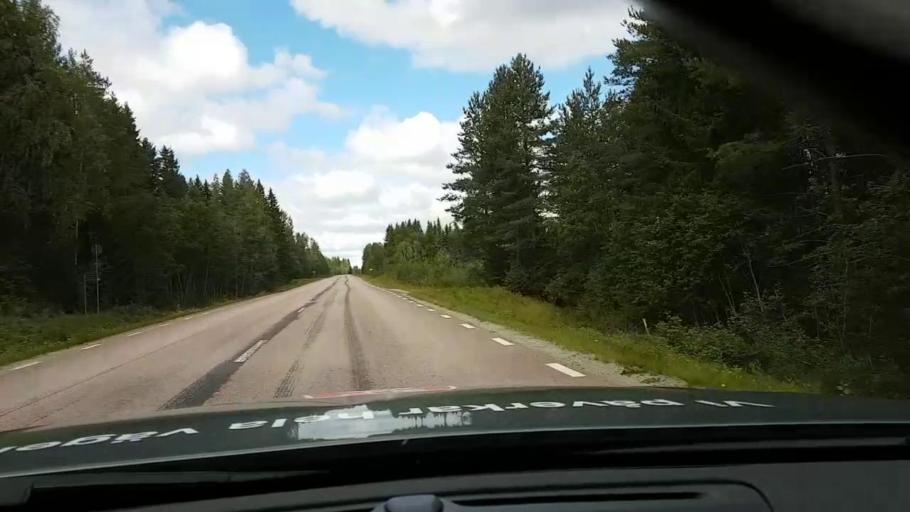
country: SE
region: Vaesternorrland
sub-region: OErnskoeldsviks Kommun
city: Bredbyn
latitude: 63.4688
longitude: 18.1018
